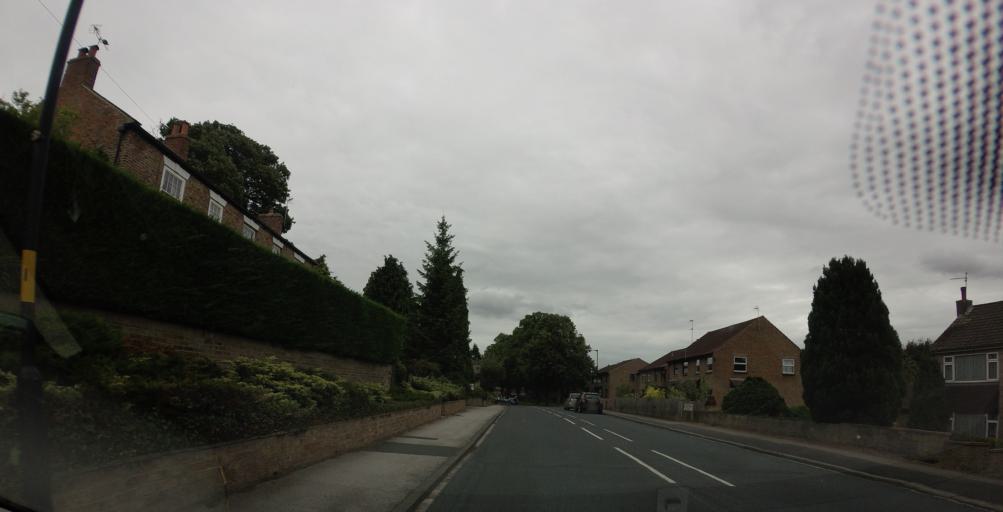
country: GB
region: England
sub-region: North Yorkshire
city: Ripon
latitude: 54.1341
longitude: -1.5294
